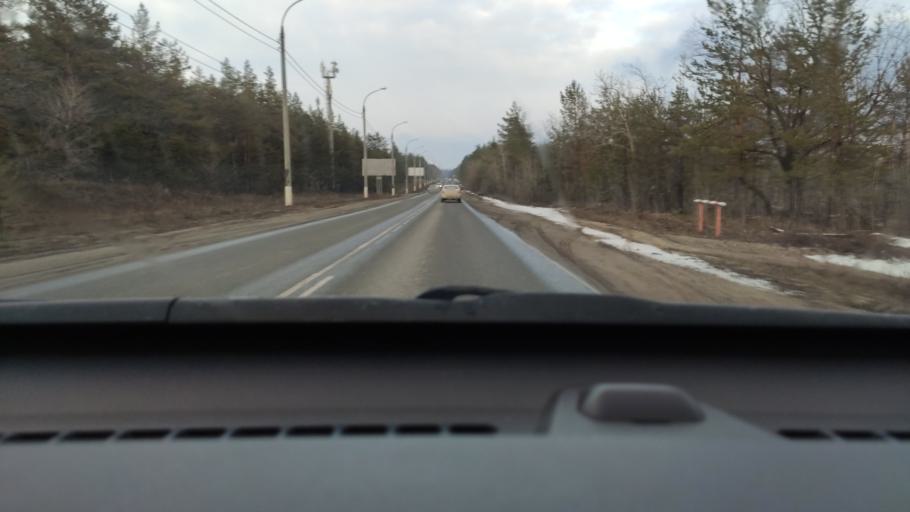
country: RU
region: Samara
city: Zhigulevsk
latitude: 53.4020
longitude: 49.5024
